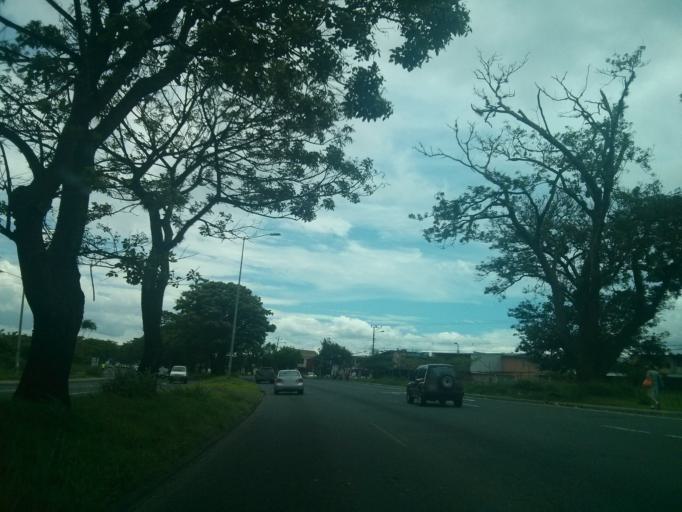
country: CR
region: San Jose
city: San Felipe
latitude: 9.9232
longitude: -84.1079
